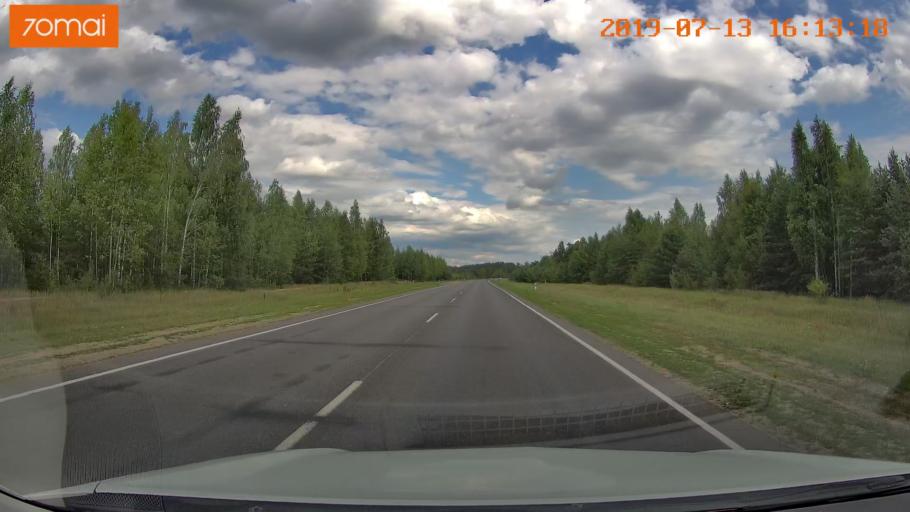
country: BY
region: Mogilev
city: Babruysk
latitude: 53.1636
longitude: 29.2999
